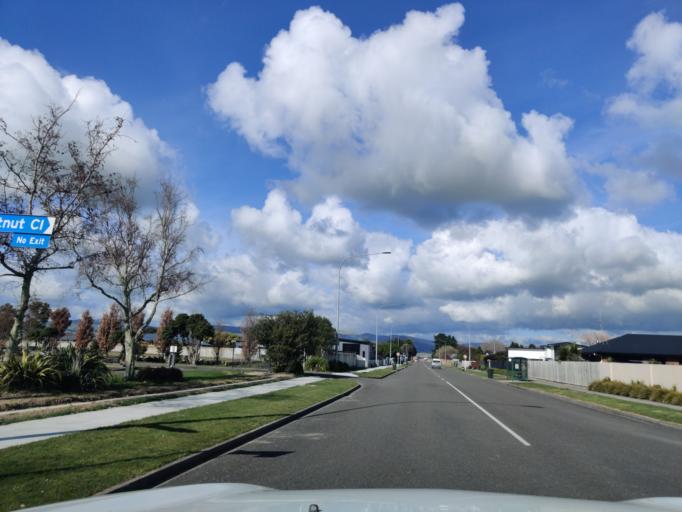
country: NZ
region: Manawatu-Wanganui
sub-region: Palmerston North City
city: Palmerston North
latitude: -40.3248
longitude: 175.6615
